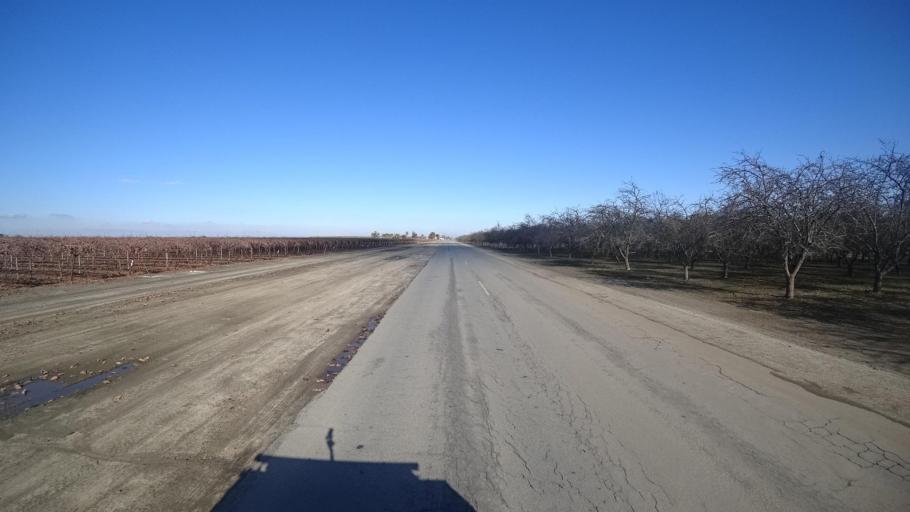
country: US
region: California
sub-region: Kern County
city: McFarland
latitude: 35.7131
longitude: -119.2586
